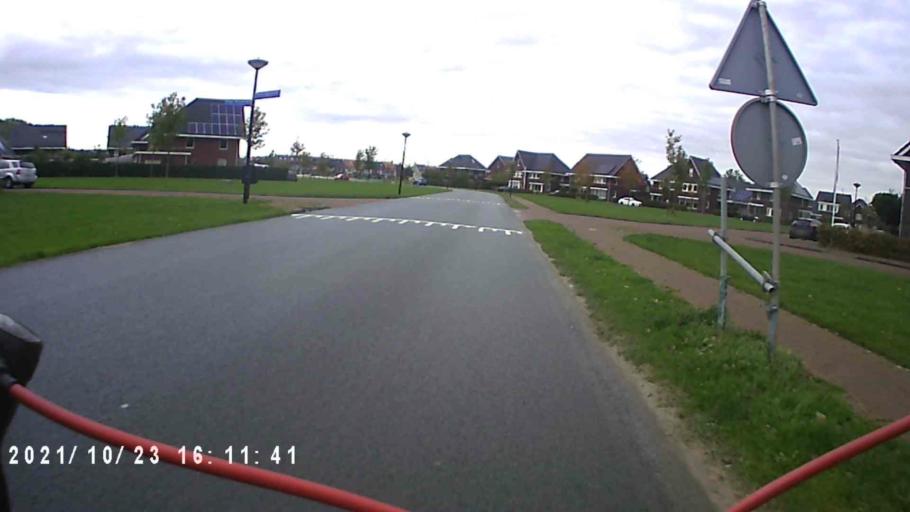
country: NL
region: North Holland
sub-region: Gemeente Langedijk
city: Broek op Langedijk
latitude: 52.6693
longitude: 4.8130
